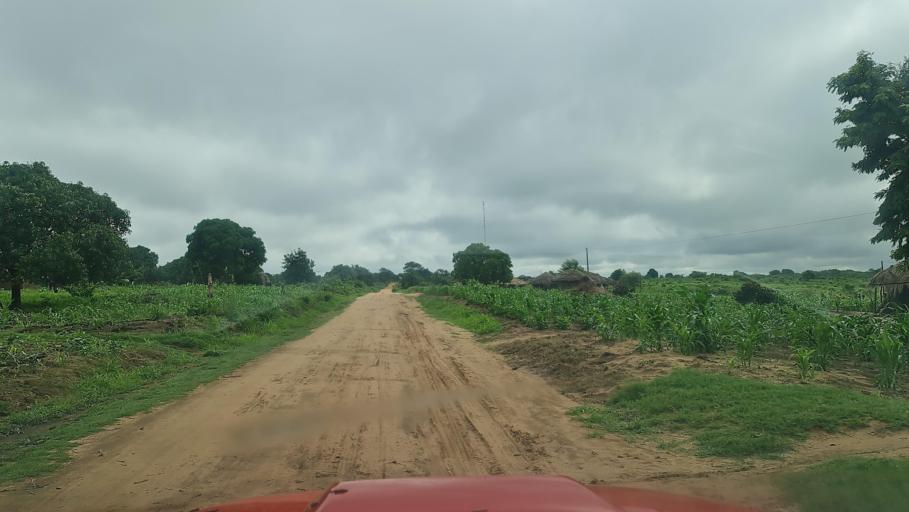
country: MW
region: Southern Region
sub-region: Nsanje District
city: Nsanje
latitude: -17.1927
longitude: 35.7029
